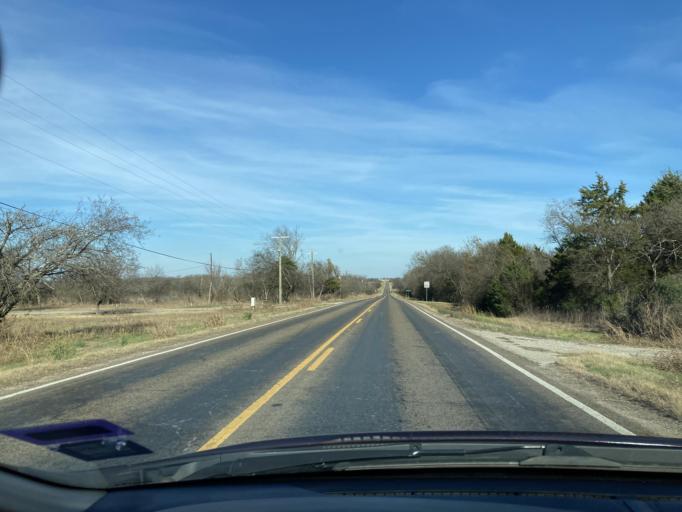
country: US
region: Texas
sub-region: Navarro County
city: Corsicana
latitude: 32.0098
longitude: -96.4321
